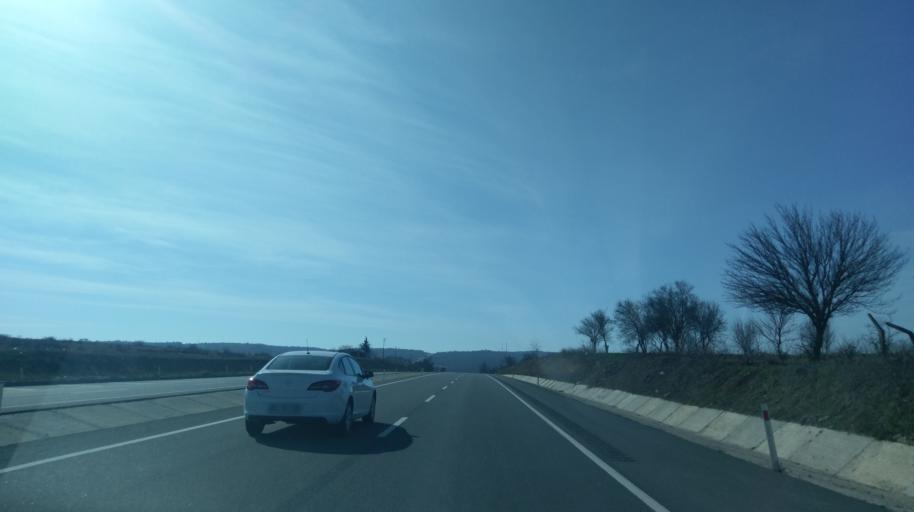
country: TR
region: Edirne
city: Ibriktepe
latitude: 40.9981
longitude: 26.6374
